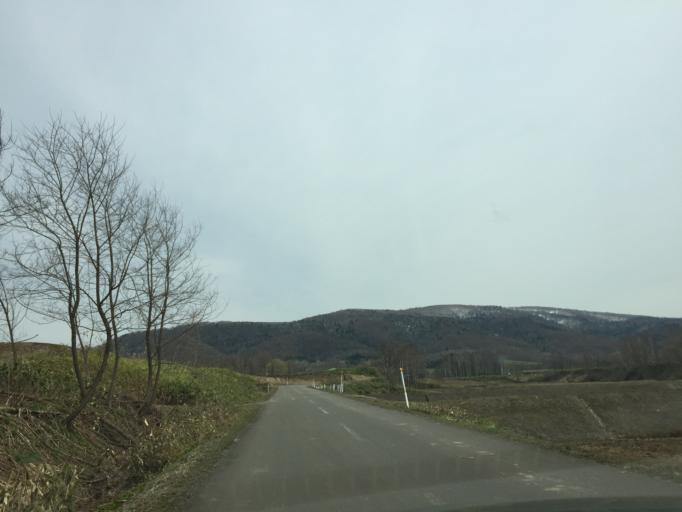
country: JP
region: Hokkaido
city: Ashibetsu
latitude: 43.6082
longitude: 142.2111
